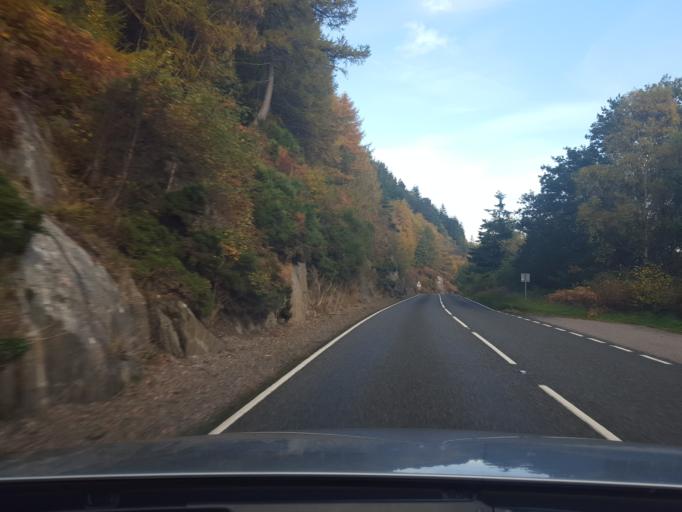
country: GB
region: Scotland
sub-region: Highland
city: Beauly
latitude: 57.3452
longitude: -4.4197
